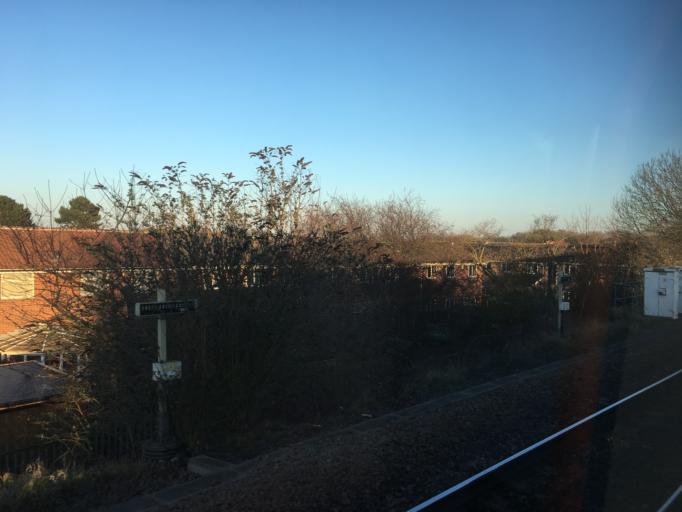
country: GB
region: England
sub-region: Derbyshire
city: Long Eaton
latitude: 52.8826
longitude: -1.2745
